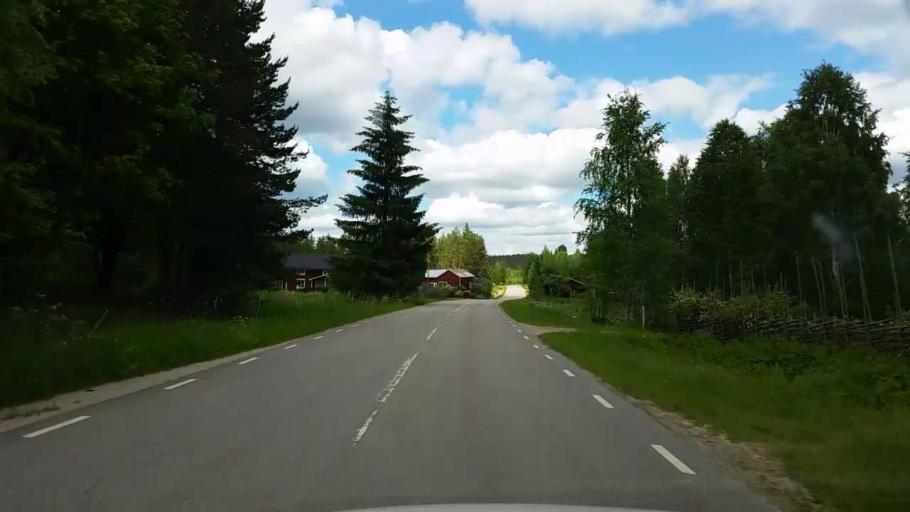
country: SE
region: Gaevleborg
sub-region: Ovanakers Kommun
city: Alfta
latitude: 61.3992
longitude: 16.0478
